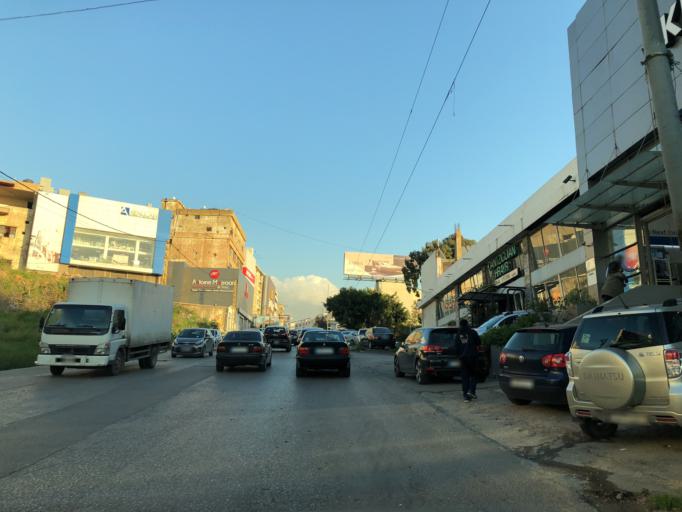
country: LB
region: Mont-Liban
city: Baabda
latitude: 33.8631
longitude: 35.5480
